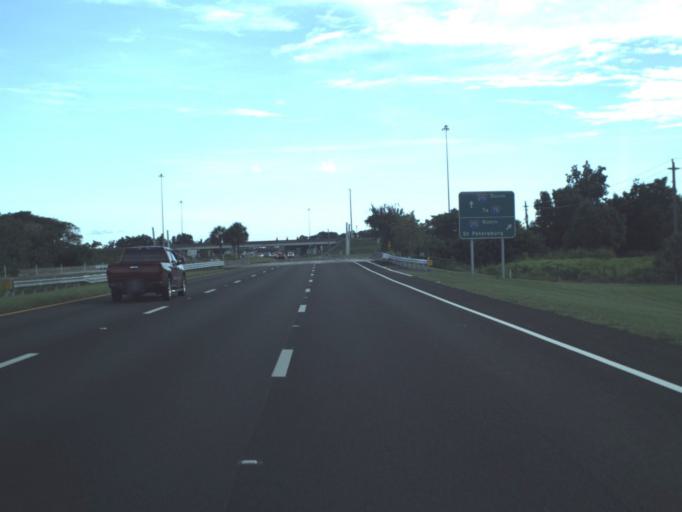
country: US
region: Florida
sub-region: Manatee County
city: Memphis
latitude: 27.5895
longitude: -82.5402
